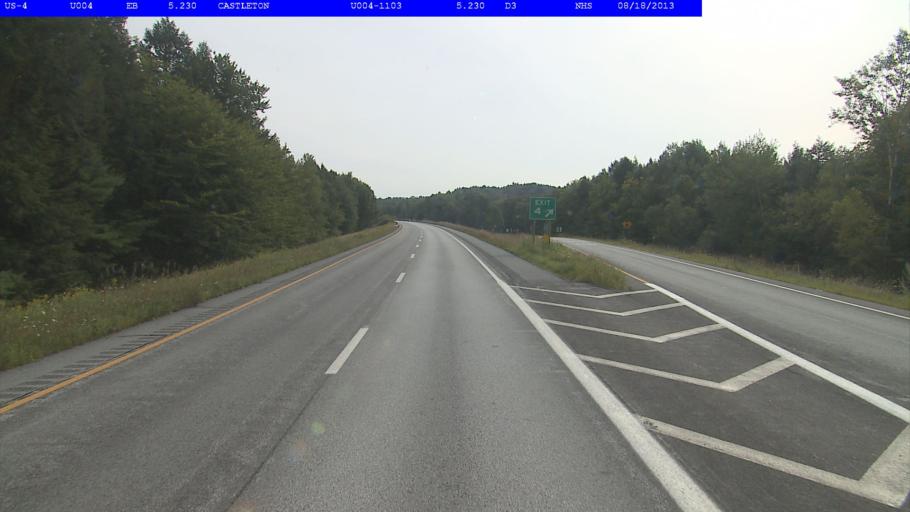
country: US
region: Vermont
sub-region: Rutland County
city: Castleton
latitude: 43.6149
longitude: -73.2107
